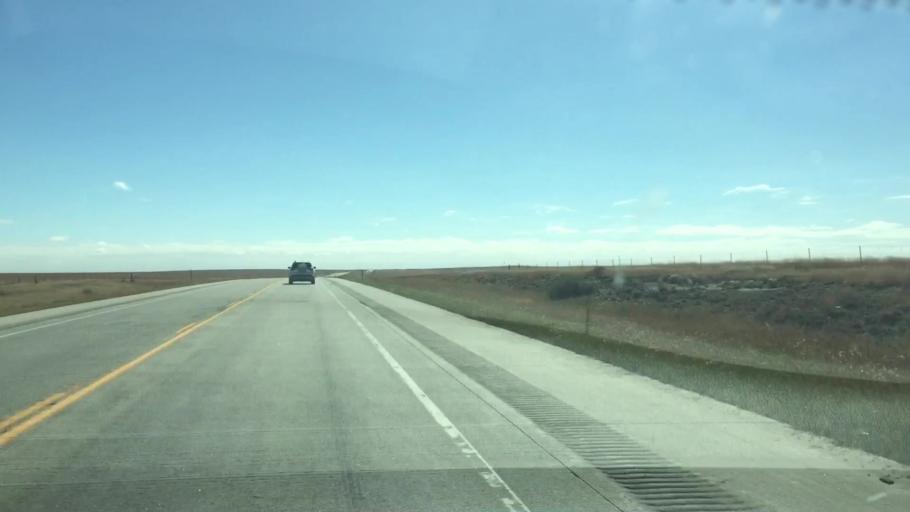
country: US
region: Colorado
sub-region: Lincoln County
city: Hugo
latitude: 39.1933
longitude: -103.5662
